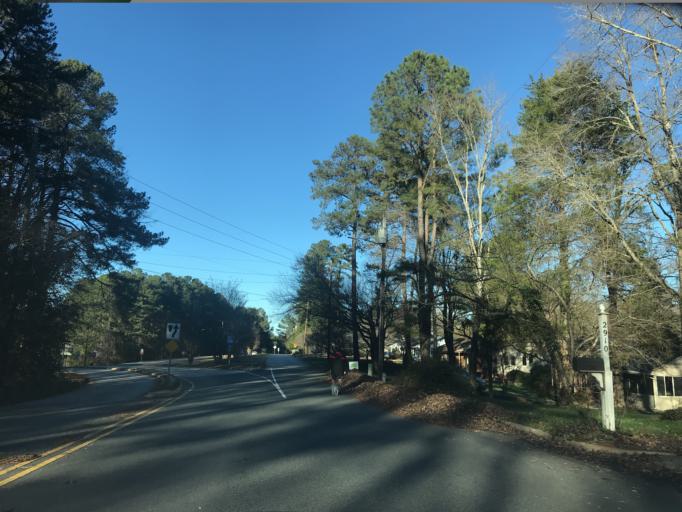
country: US
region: North Carolina
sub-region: Wake County
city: West Raleigh
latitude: 35.8311
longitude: -78.6743
